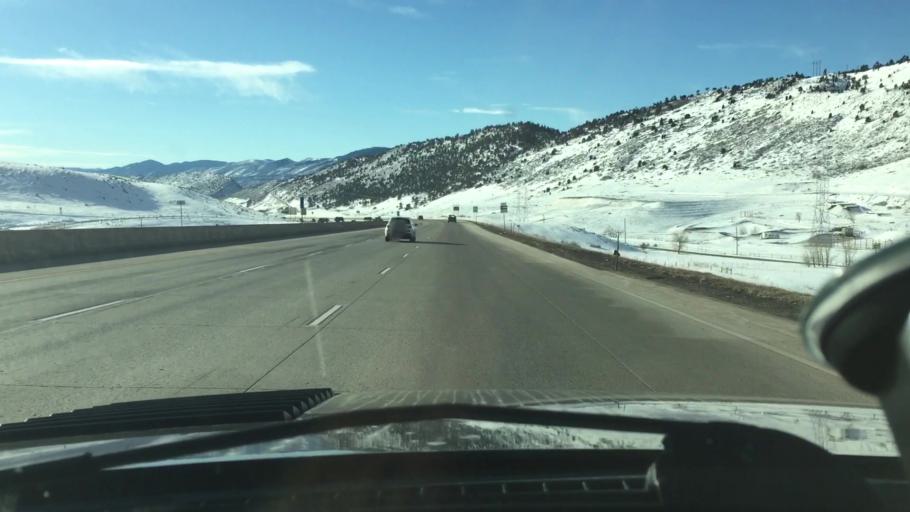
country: US
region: Colorado
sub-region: Jefferson County
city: West Pleasant View
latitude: 39.7044
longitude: -105.1933
